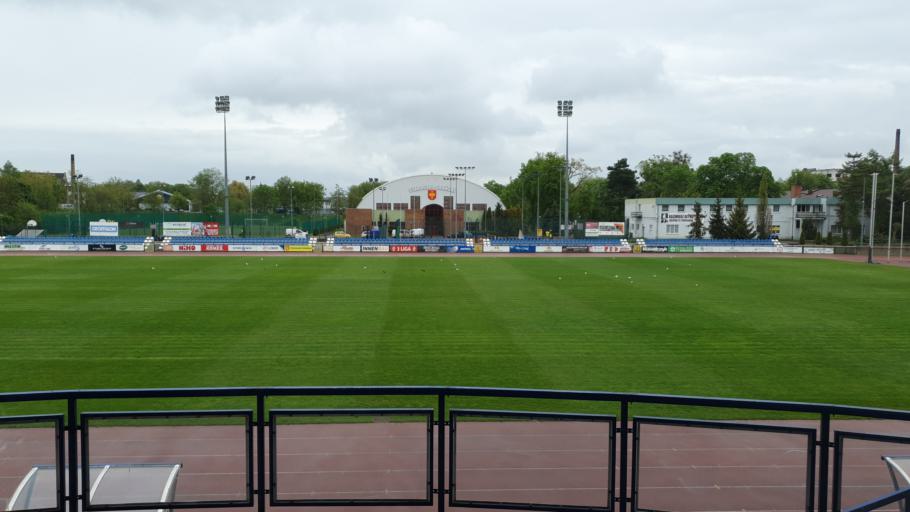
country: PL
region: Pomeranian Voivodeship
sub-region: Powiat starogardzki
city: Starogard Gdanski
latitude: 53.9705
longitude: 18.5331
